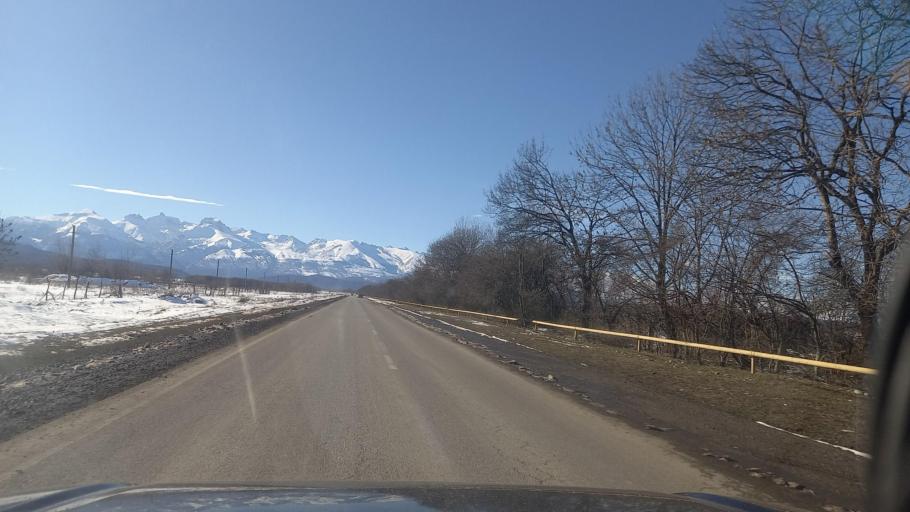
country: RU
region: North Ossetia
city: Chikola
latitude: 43.1838
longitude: 43.8953
